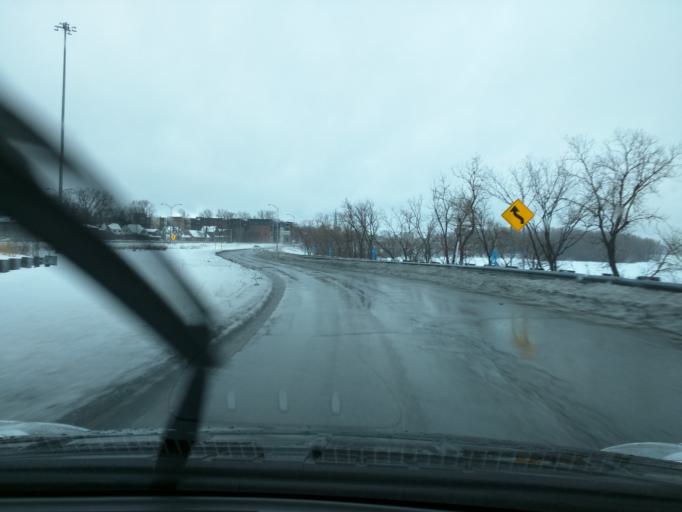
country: CA
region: Quebec
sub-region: Monteregie
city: Longueuil
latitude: 45.5498
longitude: -73.5040
